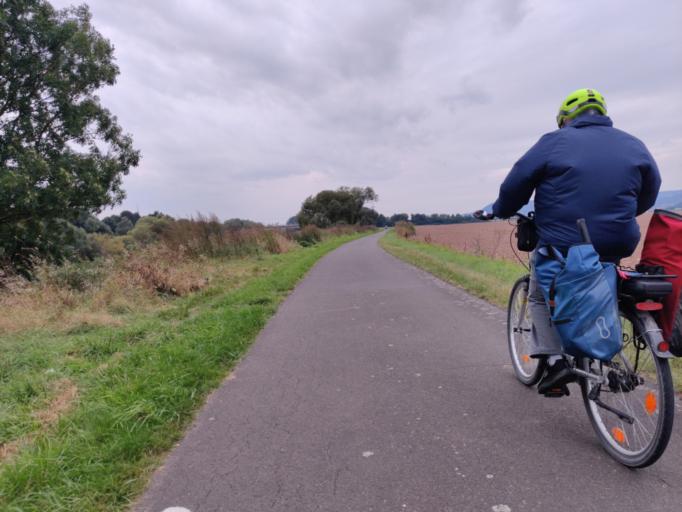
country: DE
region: Lower Saxony
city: Holzminden
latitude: 51.8038
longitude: 9.4230
